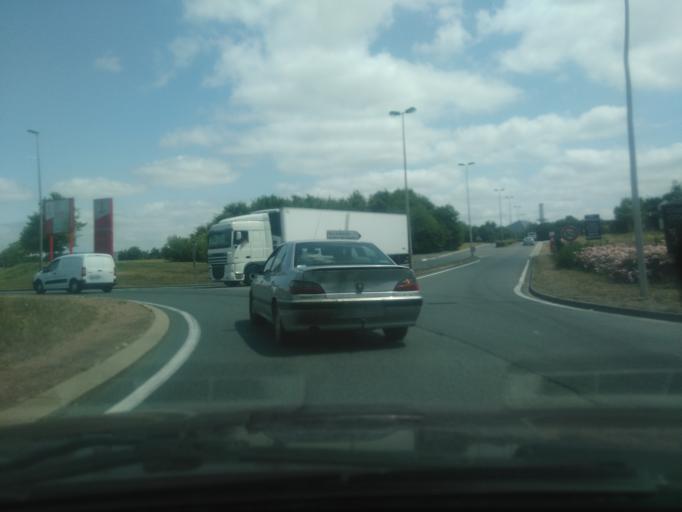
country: FR
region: Pays de la Loire
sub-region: Departement de la Vendee
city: Les Essarts
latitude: 46.7865
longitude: -1.1916
